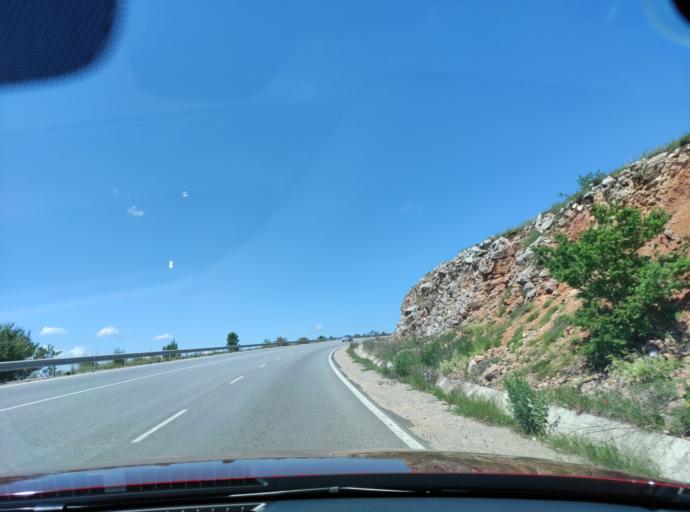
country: BG
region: Sofiya
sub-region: Obshtina Kostinbrod
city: Kostinbrod
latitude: 42.8910
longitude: 23.1560
